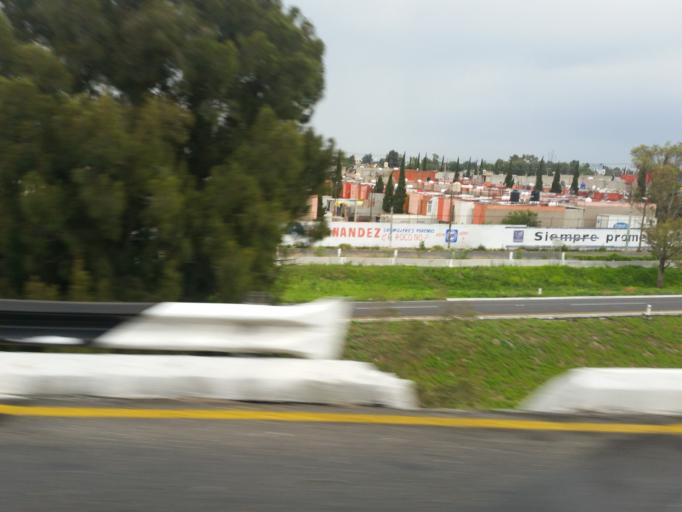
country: MX
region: Mexico
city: Ecatepec
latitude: 19.6102
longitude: -99.0330
